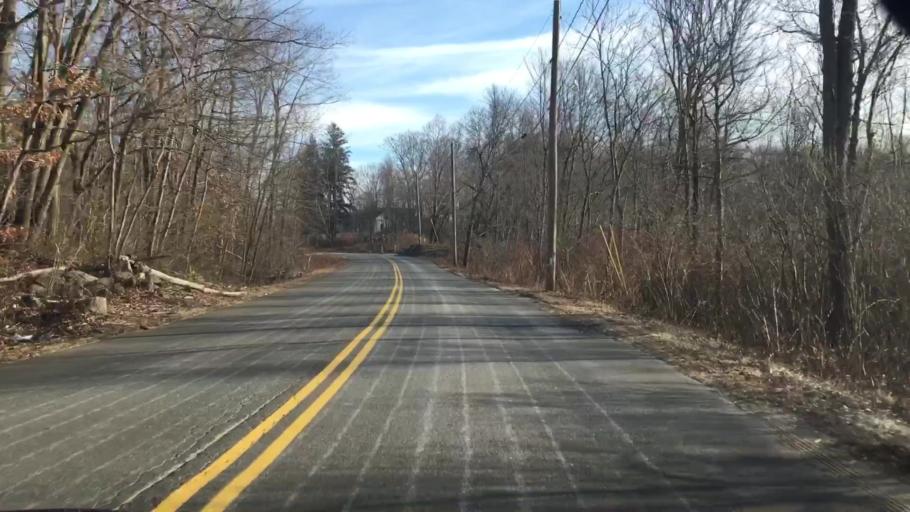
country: US
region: Connecticut
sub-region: New Haven County
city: Prospect
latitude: 41.5336
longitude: -72.9658
